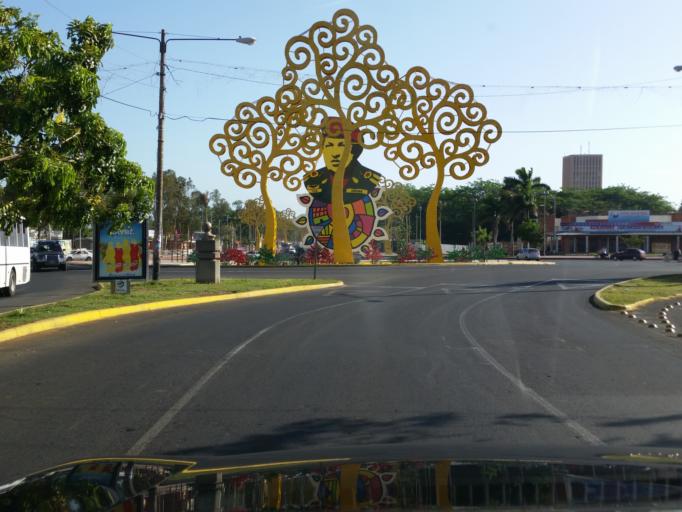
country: NI
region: Managua
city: Managua
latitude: 12.1455
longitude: -86.2747
